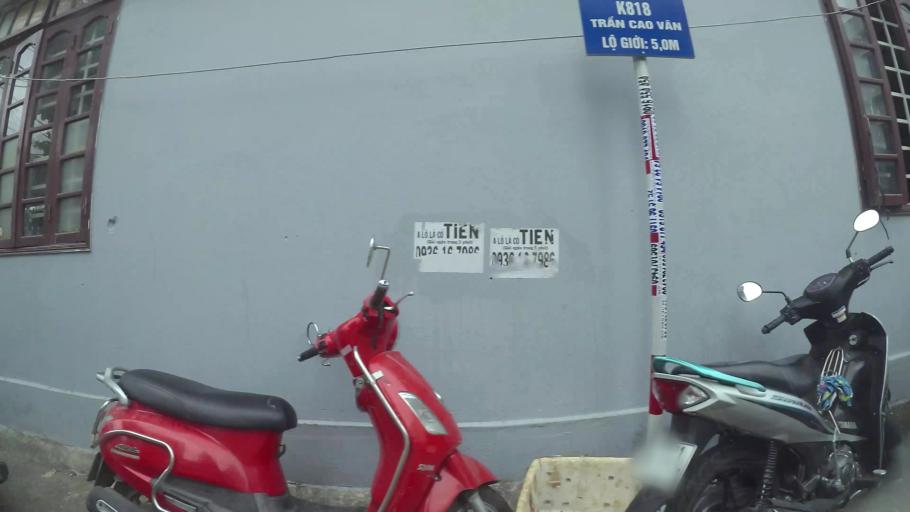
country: VN
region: Da Nang
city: Thanh Khe
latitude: 16.0699
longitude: 108.1845
